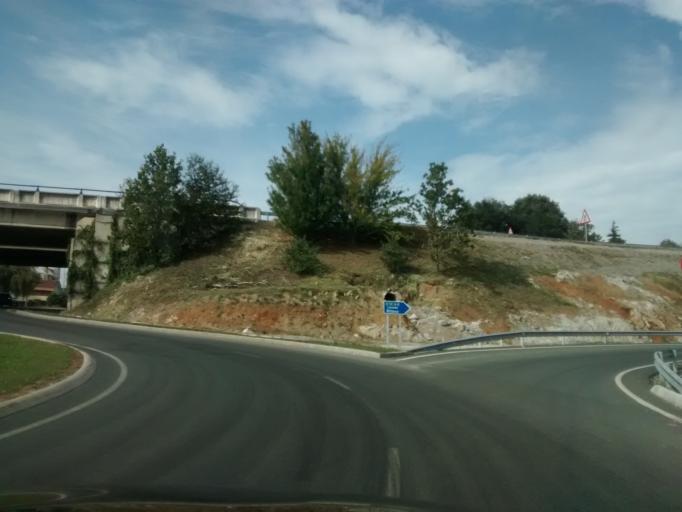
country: ES
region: Cantabria
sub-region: Provincia de Cantabria
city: Lierganes
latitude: 43.3853
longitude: -3.7416
